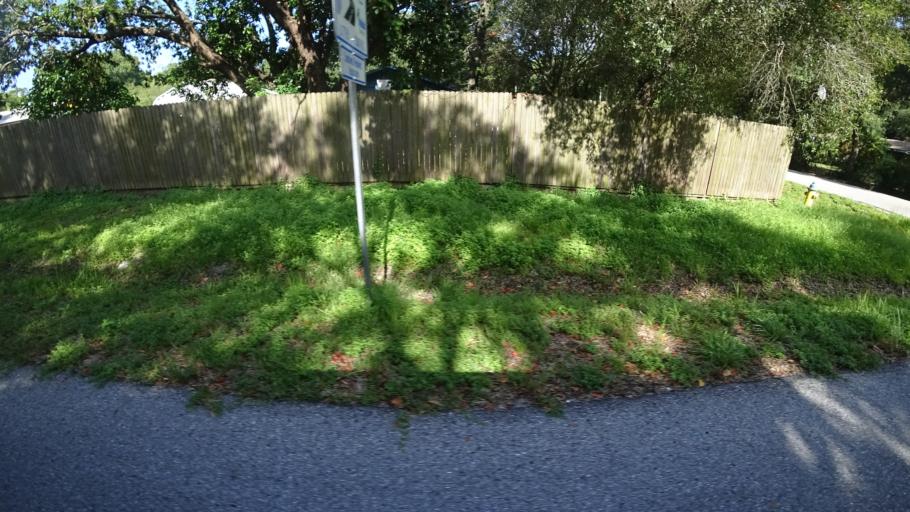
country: US
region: Florida
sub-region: Manatee County
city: West Samoset
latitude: 27.4429
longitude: -82.5493
